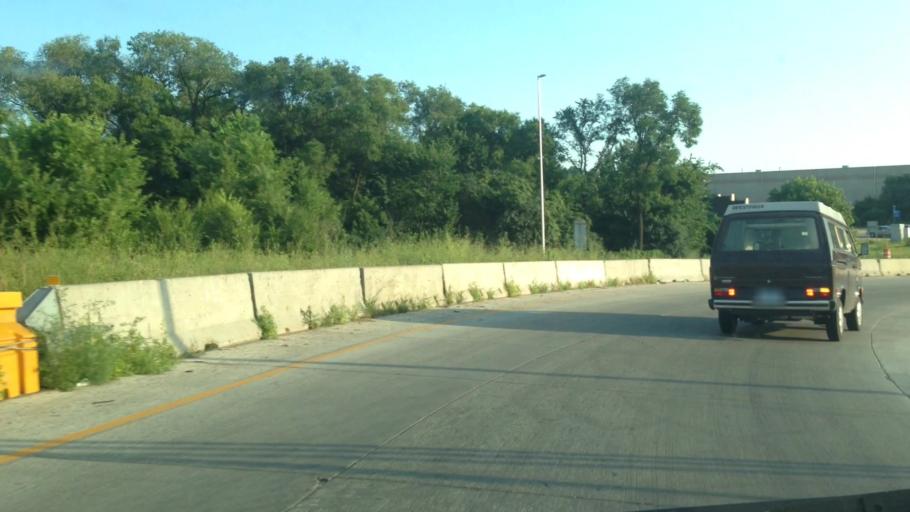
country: US
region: Minnesota
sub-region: Hennepin County
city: Brooklyn Park
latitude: 45.0772
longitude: -93.3713
